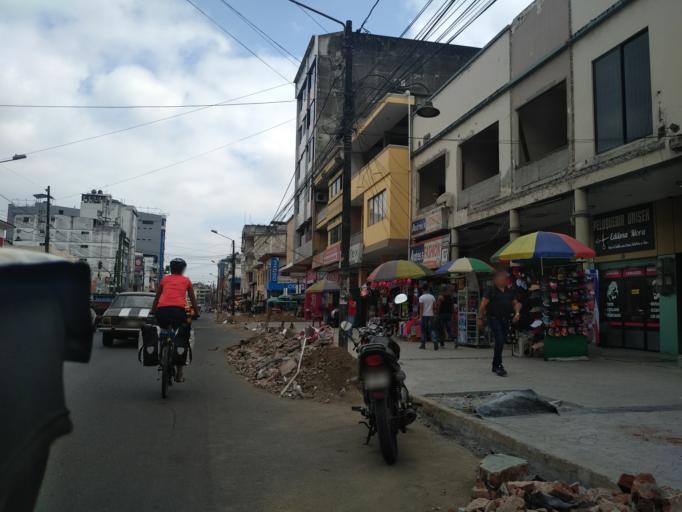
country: EC
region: Los Rios
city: Quevedo
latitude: -1.0270
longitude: -79.4676
